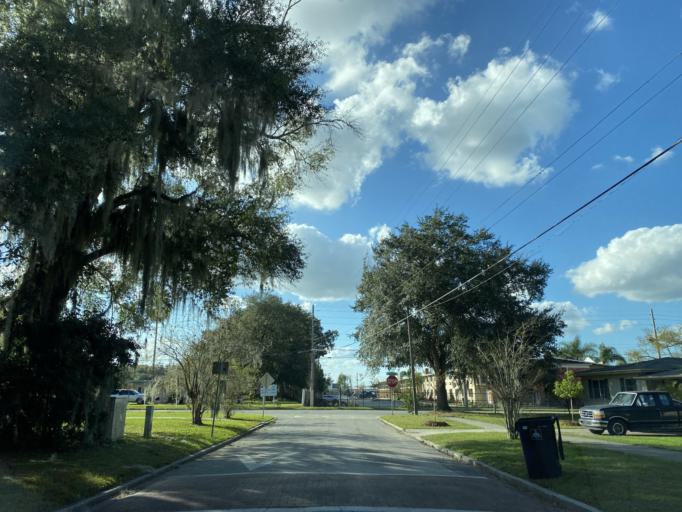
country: US
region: Florida
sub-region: Orange County
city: Orlando
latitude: 28.5518
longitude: -81.4051
